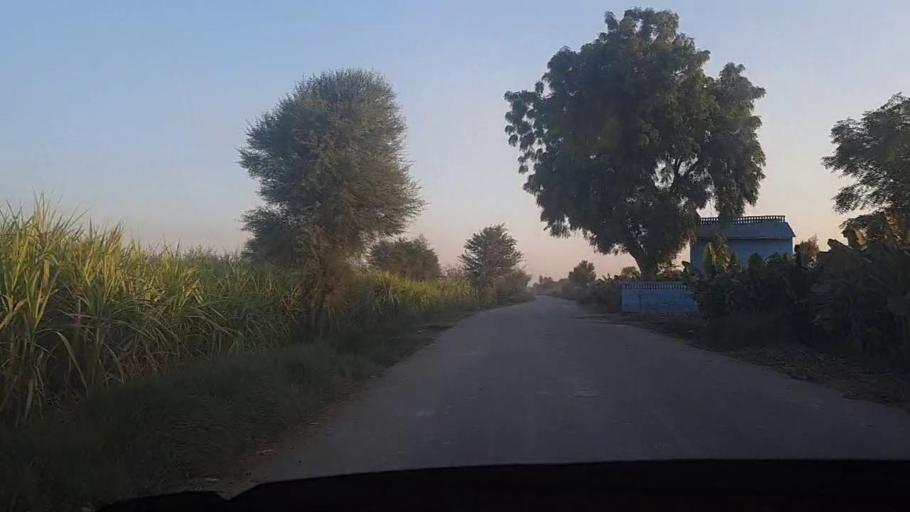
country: PK
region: Sindh
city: Sobhadero
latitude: 27.3468
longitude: 68.3760
